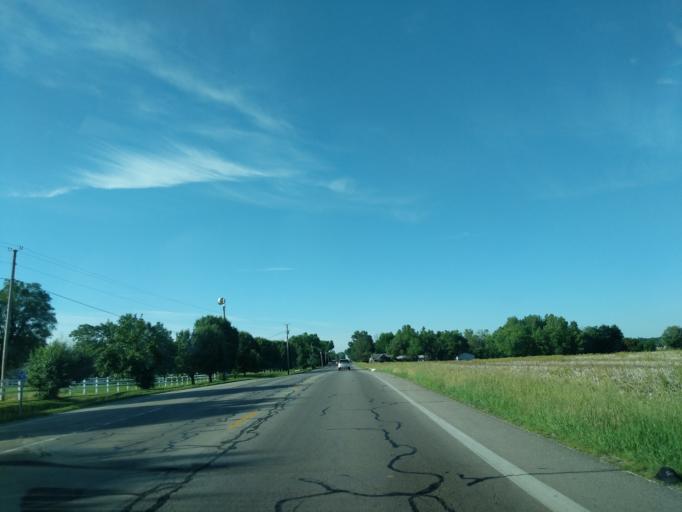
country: US
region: Indiana
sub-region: Hancock County
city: Greenfield
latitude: 39.8532
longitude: -85.7700
